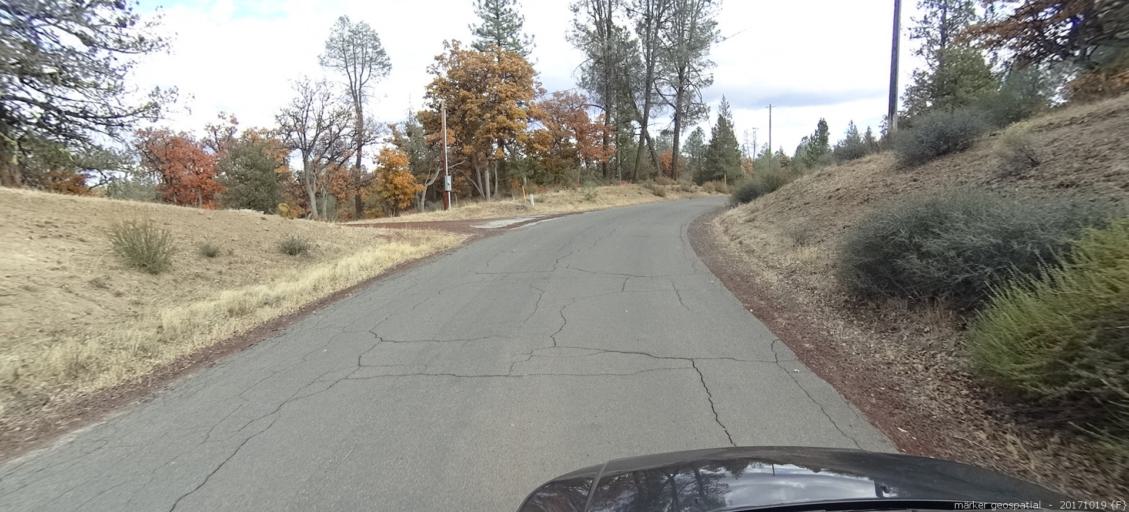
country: US
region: California
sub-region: Shasta County
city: Burney
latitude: 40.9774
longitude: -121.4442
